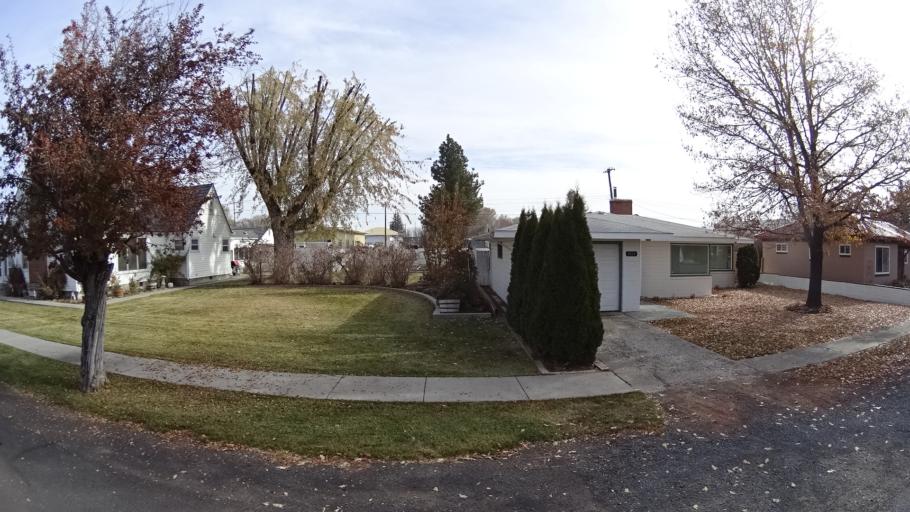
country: US
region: California
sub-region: Siskiyou County
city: Tulelake
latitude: 41.9532
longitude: -121.4780
